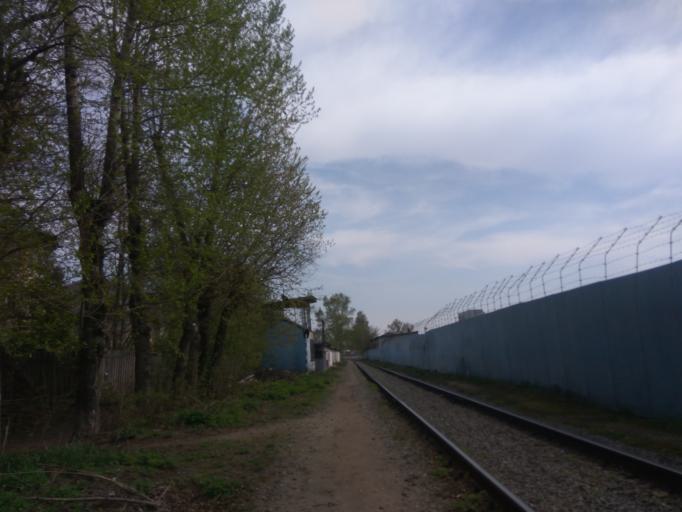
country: RU
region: Moskovskaya
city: Bykovo
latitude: 55.6254
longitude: 38.0629
